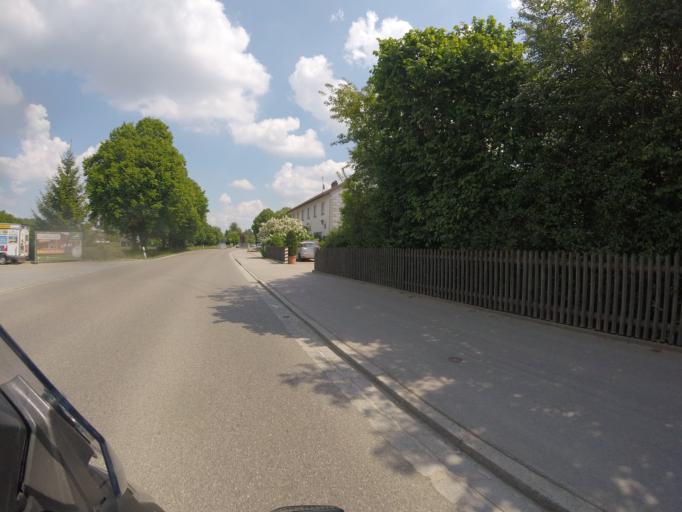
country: DE
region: Bavaria
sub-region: Upper Bavaria
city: Scheyern
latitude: 48.5180
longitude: 11.4614
